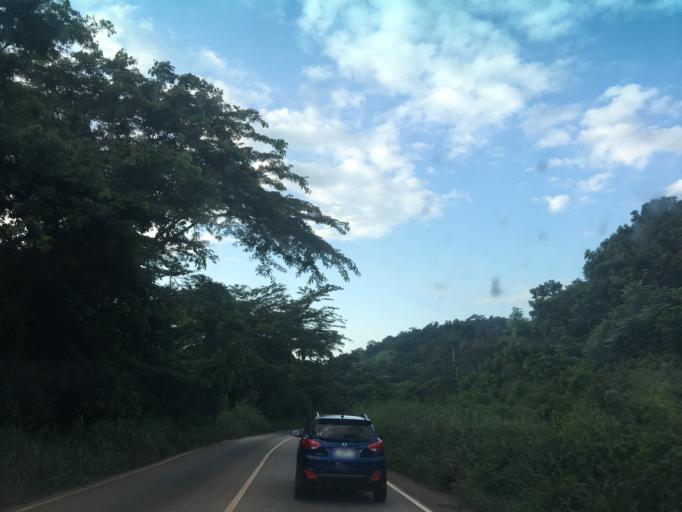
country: GH
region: Western
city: Bibiani
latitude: 6.4758
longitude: -2.3331
